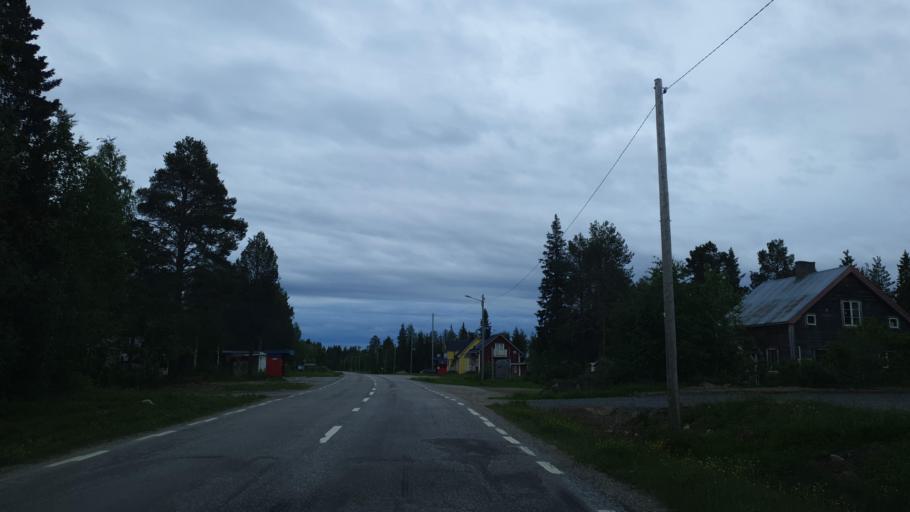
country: SE
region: Norrbotten
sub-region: Jokkmokks Kommun
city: Jokkmokk
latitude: 66.1554
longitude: 19.9806
